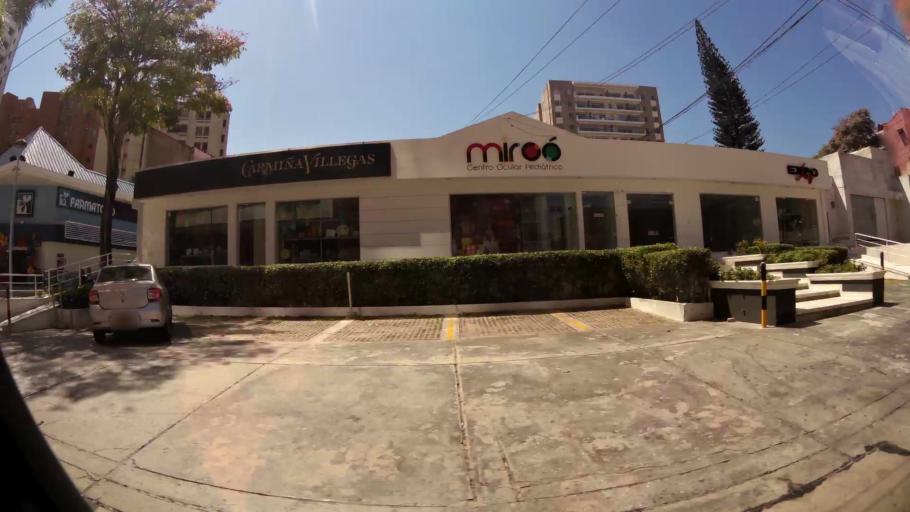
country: CO
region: Atlantico
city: Barranquilla
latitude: 11.0042
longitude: -74.8137
